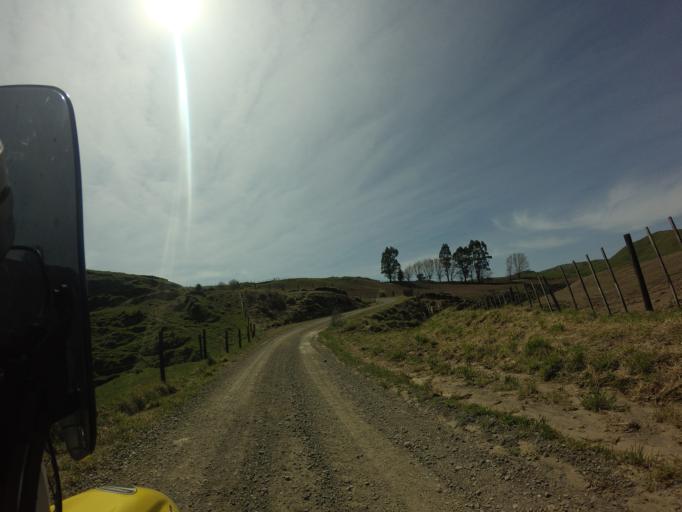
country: NZ
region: Bay of Plenty
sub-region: Opotiki District
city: Opotiki
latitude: -38.4610
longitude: 177.3805
